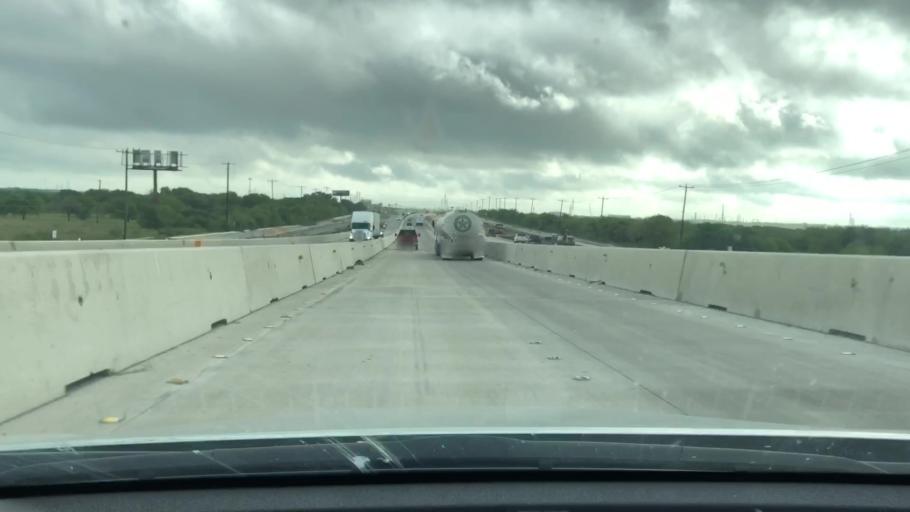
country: US
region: Texas
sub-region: Bexar County
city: Kirby
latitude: 29.4505
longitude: -98.3413
